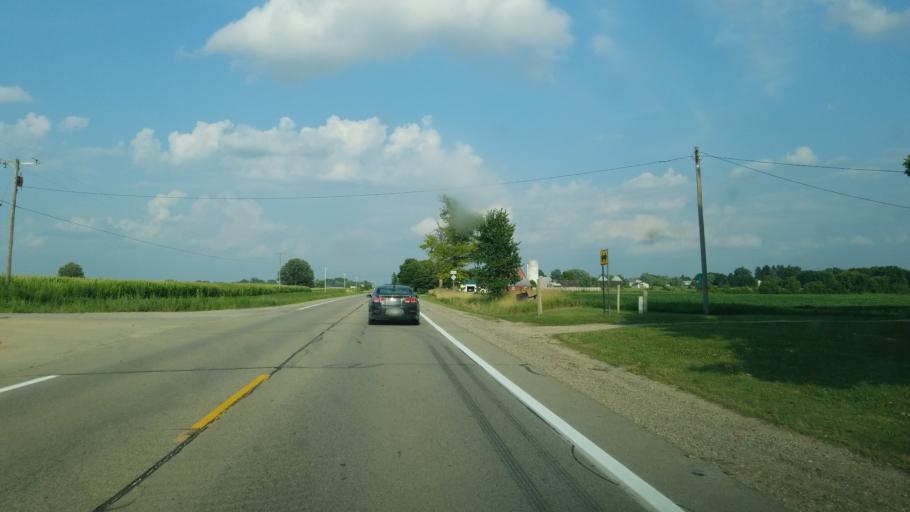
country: US
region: Michigan
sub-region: Gratiot County
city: Alma
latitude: 43.4081
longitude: -84.6970
